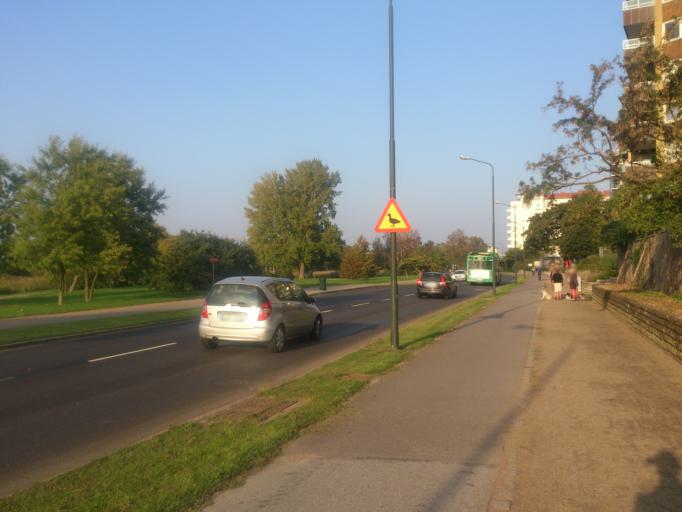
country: SE
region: Skane
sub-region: Malmo
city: Malmoe
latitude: 55.6017
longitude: 12.9701
